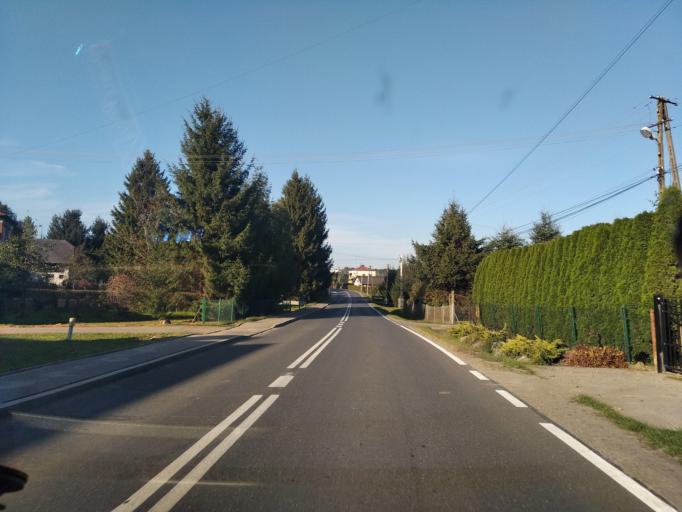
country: PL
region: Subcarpathian Voivodeship
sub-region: Powiat brzozowski
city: Humniska
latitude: 49.6794
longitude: 22.0340
